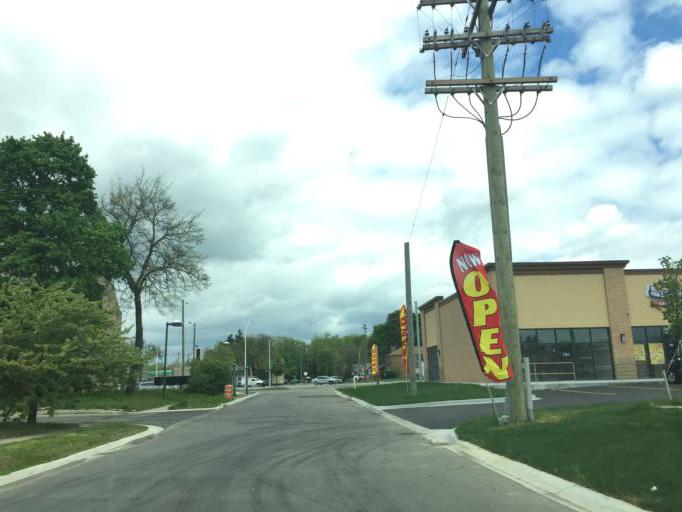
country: US
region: Michigan
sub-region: Wayne County
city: Redford
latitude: 42.4141
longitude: -83.2539
